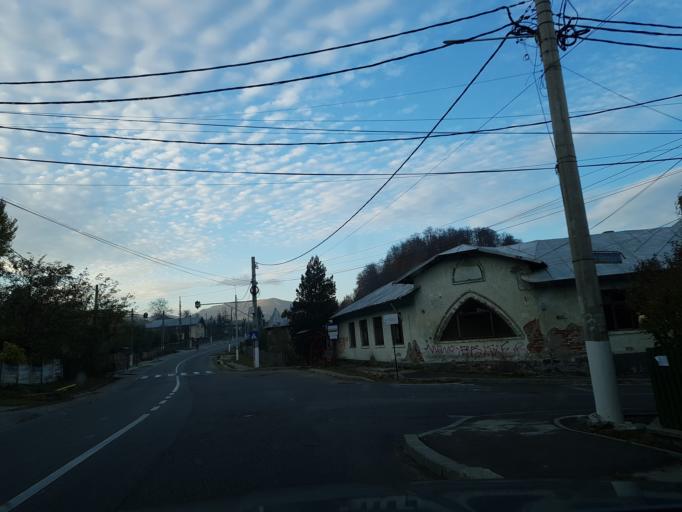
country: RO
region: Prahova
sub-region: Oras Breaza
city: Gura Beliei
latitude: 45.2099
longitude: 25.6474
